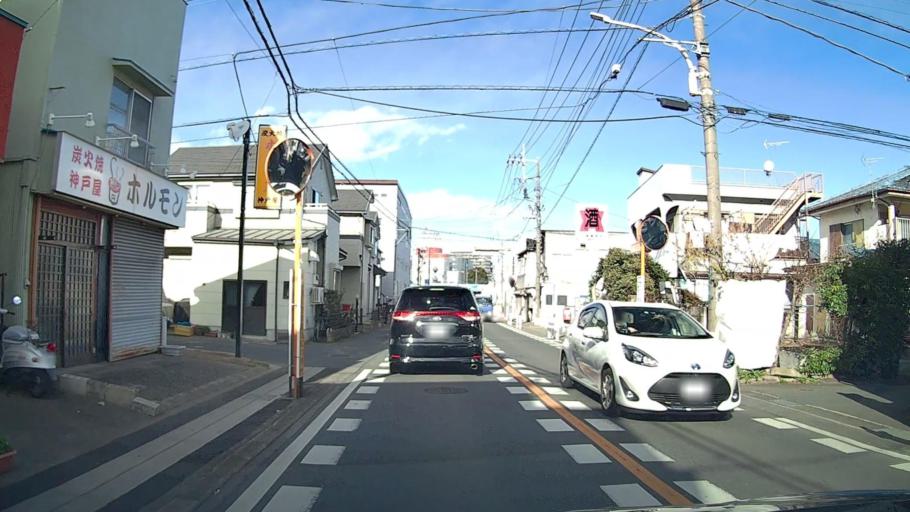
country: JP
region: Saitama
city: Asaka
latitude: 35.7920
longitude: 139.5759
